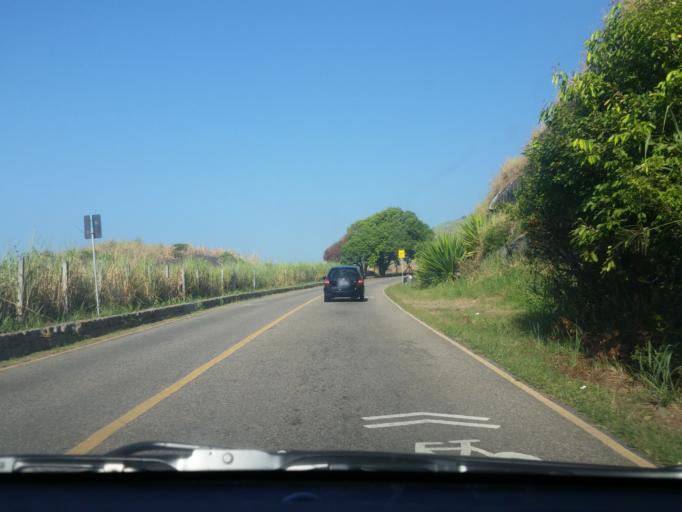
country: BR
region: Rio de Janeiro
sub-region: Nilopolis
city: Nilopolis
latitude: -23.0348
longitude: -43.4940
